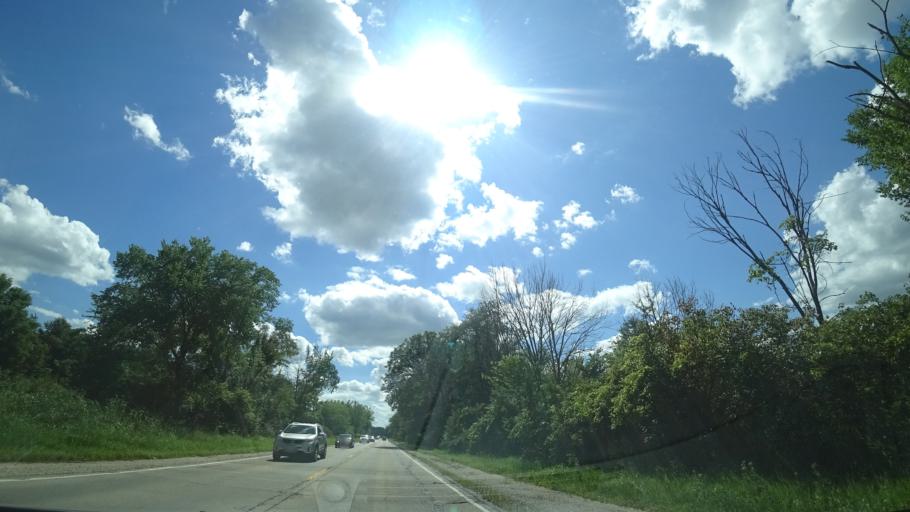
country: US
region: Illinois
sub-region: Will County
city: Mokena
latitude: 41.5528
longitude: -87.9242
